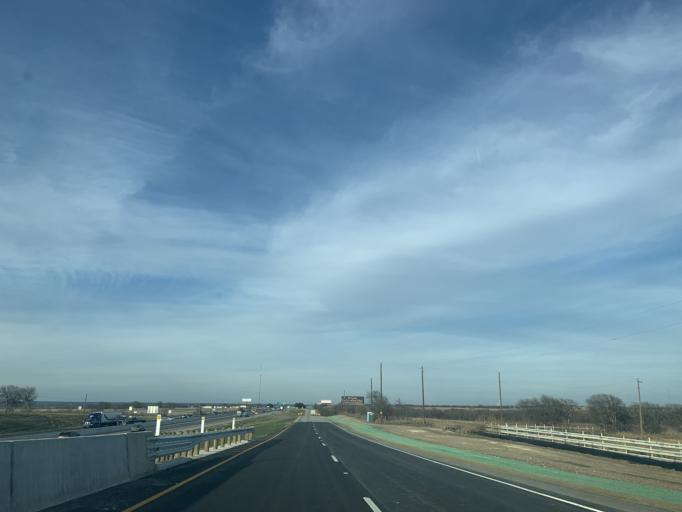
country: US
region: Texas
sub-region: Bell County
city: Salado
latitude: 30.8455
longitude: -97.5940
